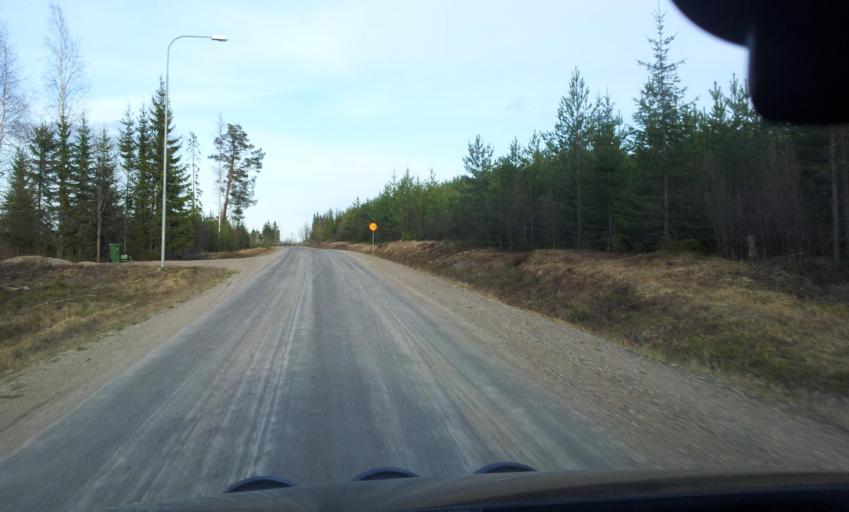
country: SE
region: Gaevleborg
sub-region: Ljusdals Kommun
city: Farila
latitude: 62.1139
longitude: 15.6945
